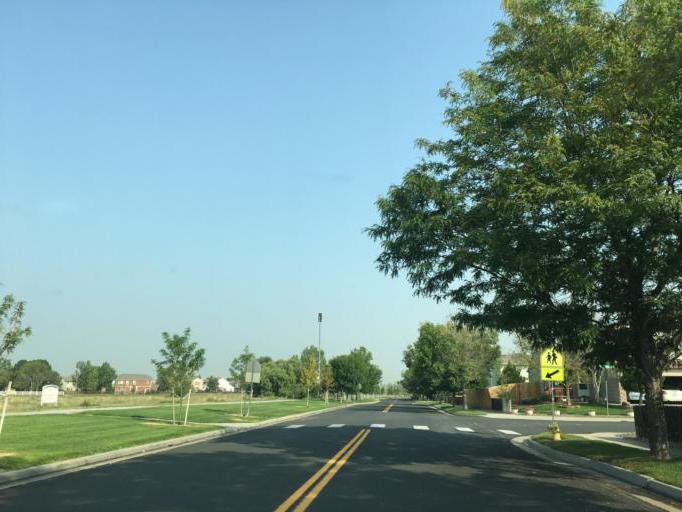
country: US
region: Colorado
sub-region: Adams County
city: Todd Creek
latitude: 39.9036
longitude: -104.8549
